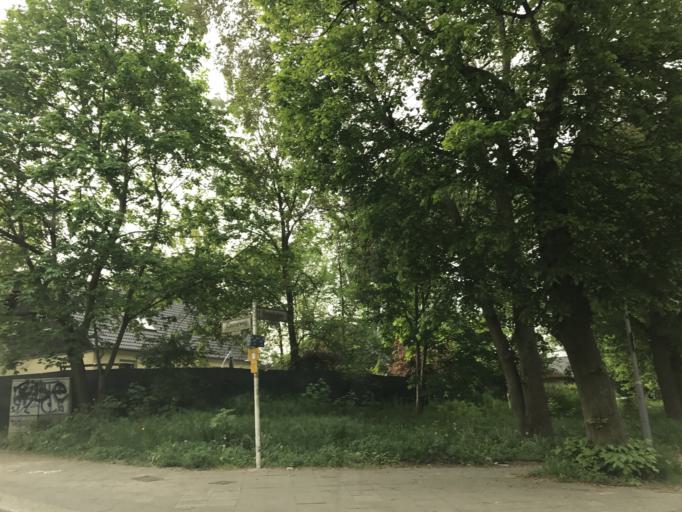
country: DE
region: Berlin
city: Staaken
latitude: 52.5278
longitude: 13.1442
